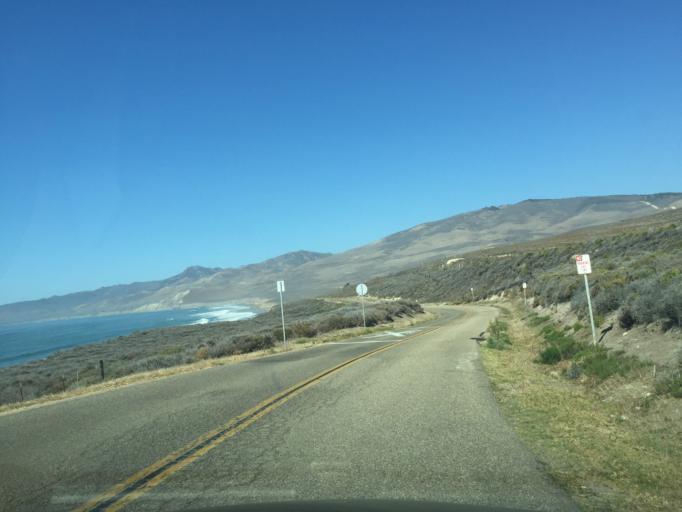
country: US
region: California
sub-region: Santa Barbara County
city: Lompoc
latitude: 34.5020
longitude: -120.4974
